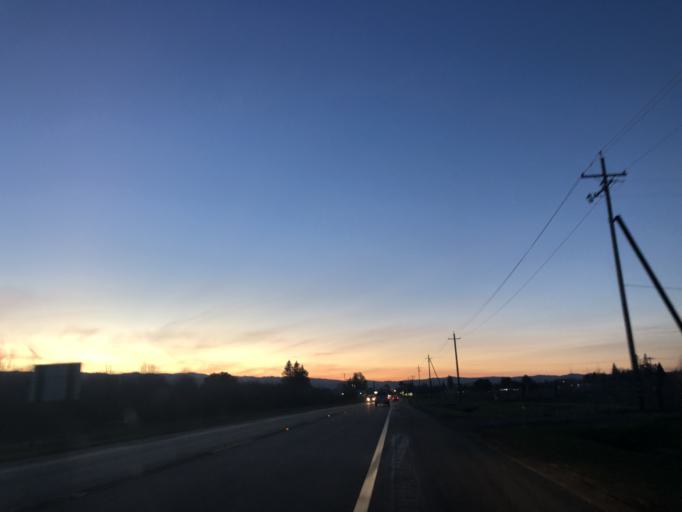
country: US
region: California
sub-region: Yolo County
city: Esparto
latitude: 38.6878
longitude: -122.0087
